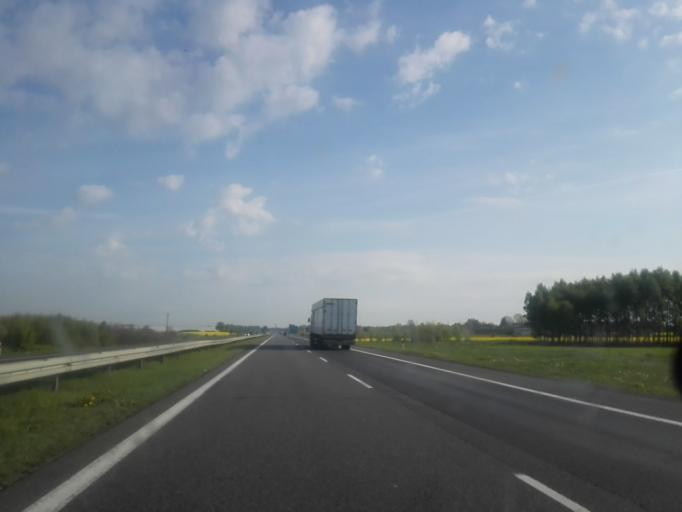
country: PL
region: Lodz Voivodeship
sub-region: Piotrkow Trybunalski
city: Piotrkow Trybunalski
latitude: 51.3974
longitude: 19.6309
